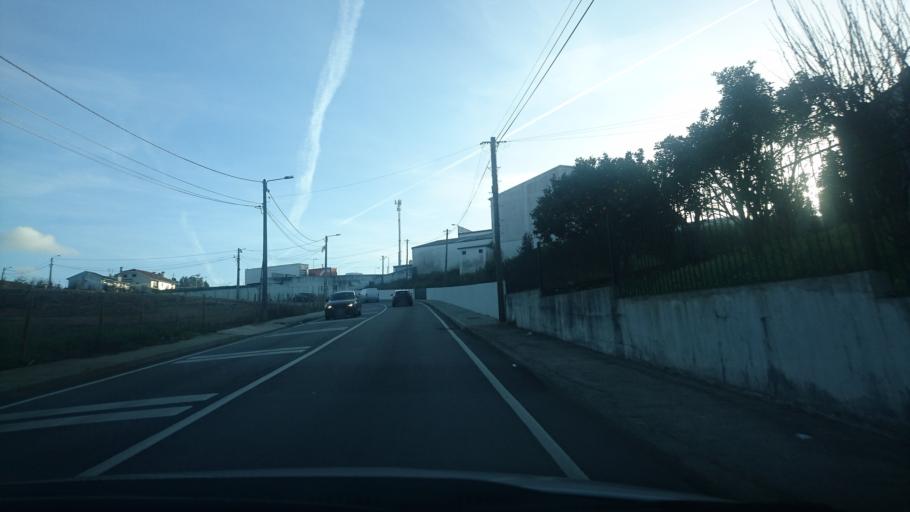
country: PT
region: Aveiro
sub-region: Espinho
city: Souto
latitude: 40.9741
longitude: -8.6078
